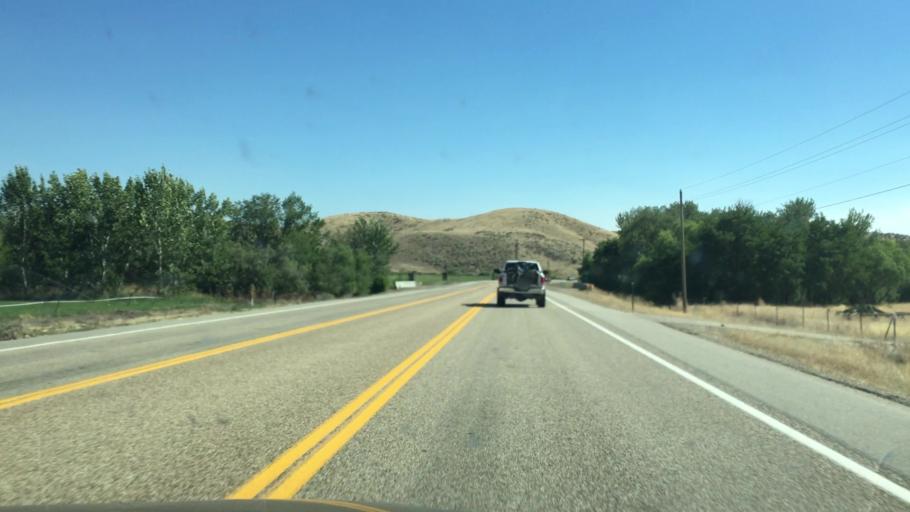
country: US
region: Idaho
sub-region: Ada County
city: Eagle
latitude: 43.7336
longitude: -116.3042
